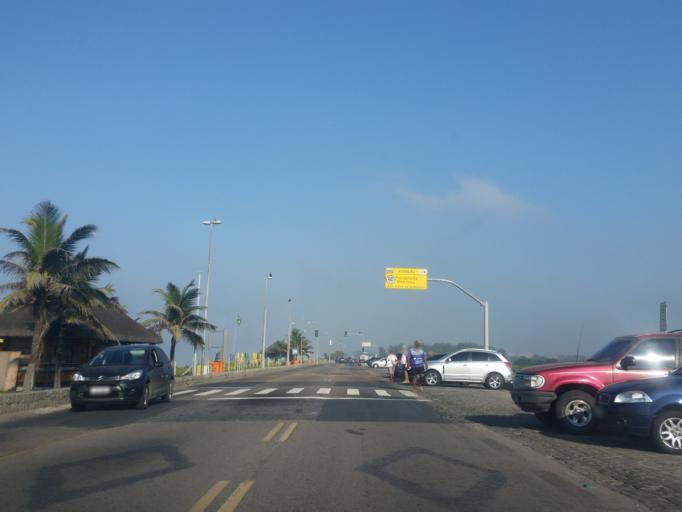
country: BR
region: Rio de Janeiro
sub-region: Nilopolis
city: Nilopolis
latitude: -23.0123
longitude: -43.3850
